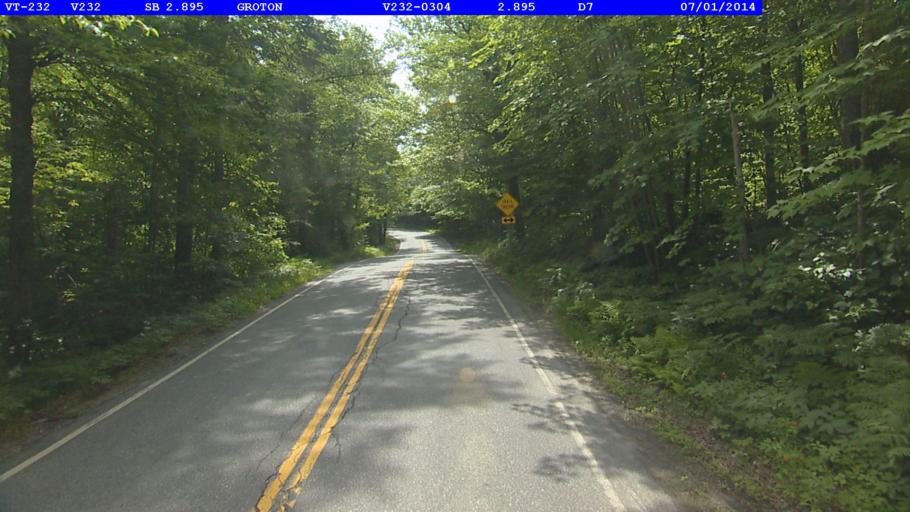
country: US
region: New Hampshire
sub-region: Grafton County
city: Woodsville
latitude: 44.2483
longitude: -72.2601
